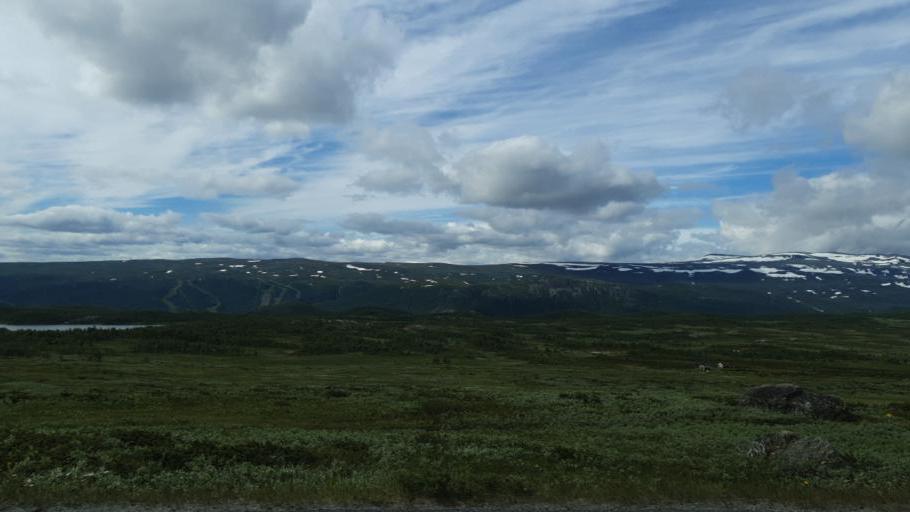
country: NO
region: Oppland
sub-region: Vestre Slidre
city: Slidre
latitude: 61.2728
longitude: 8.8588
